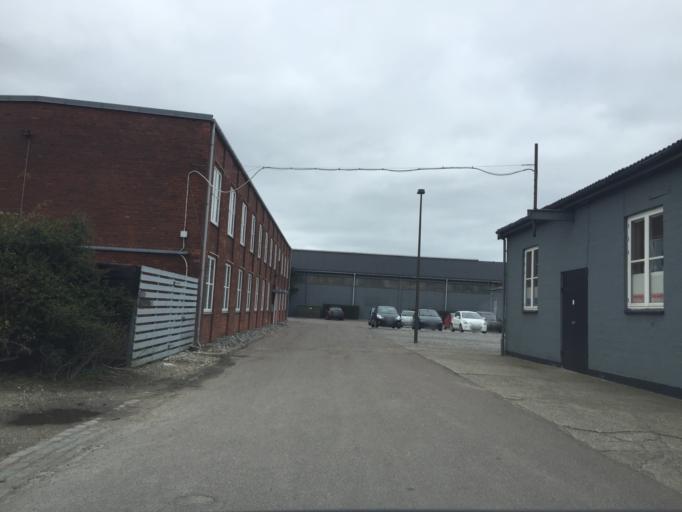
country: DK
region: Capital Region
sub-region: Gentofte Kommune
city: Charlottenlund
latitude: 55.7153
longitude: 12.6012
